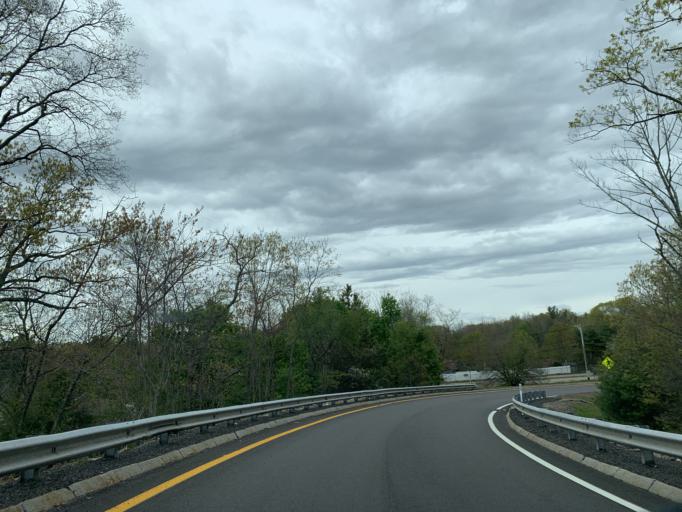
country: US
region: Massachusetts
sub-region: Bristol County
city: Attleboro
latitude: 41.9325
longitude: -71.3227
